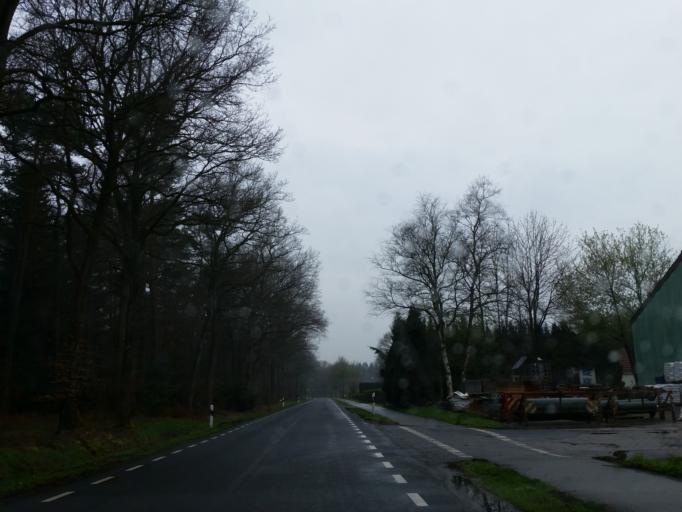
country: DE
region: Lower Saxony
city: Hipstedt
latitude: 53.5207
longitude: 8.9634
